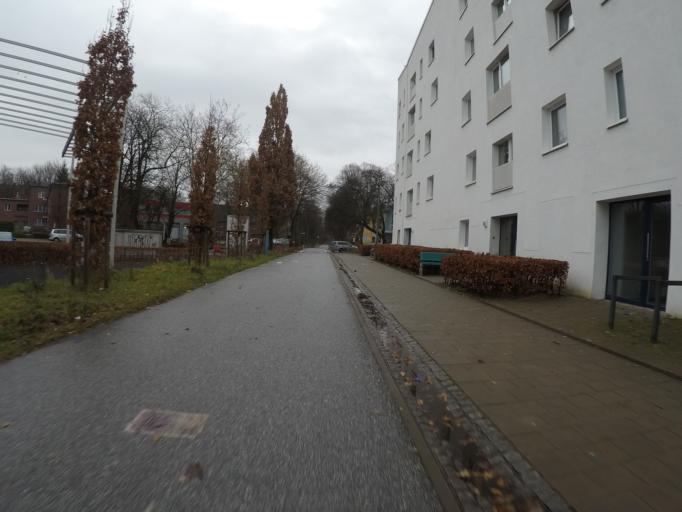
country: DE
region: Hamburg
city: Kleiner Grasbrook
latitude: 53.5060
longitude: 9.9870
